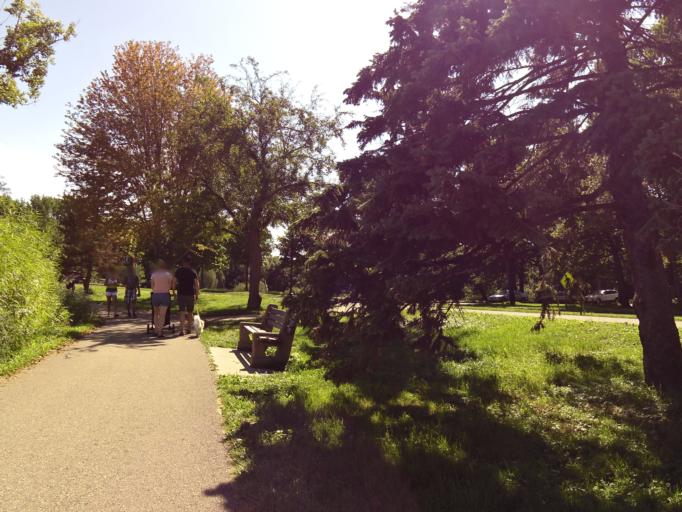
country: US
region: Minnesota
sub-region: Hennepin County
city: Saint Louis Park
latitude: 44.9525
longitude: -93.3117
